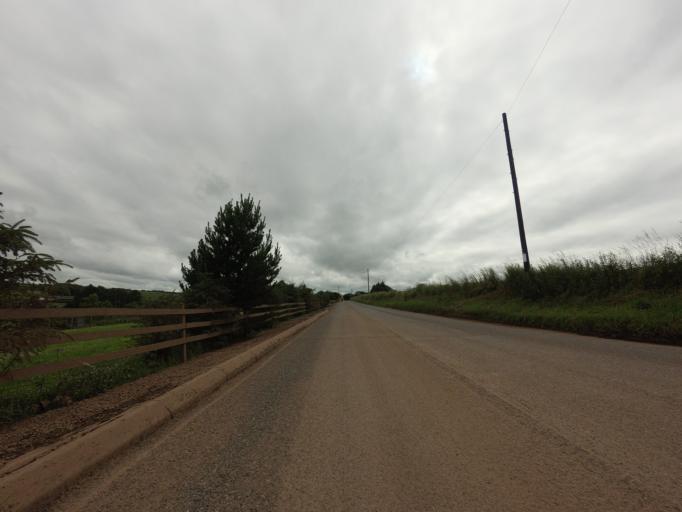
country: GB
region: Scotland
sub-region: Aberdeenshire
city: Turriff
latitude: 57.5413
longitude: -2.3666
